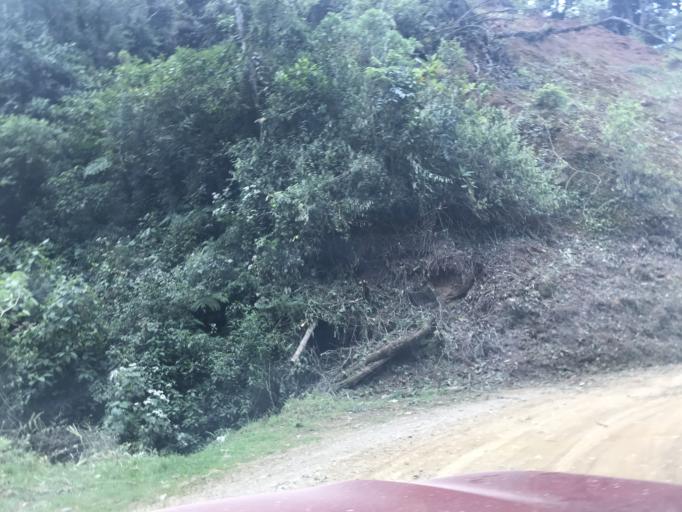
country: PE
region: Cajamarca
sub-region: Provincia de Chota
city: Querocoto
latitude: -6.3511
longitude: -79.0587
